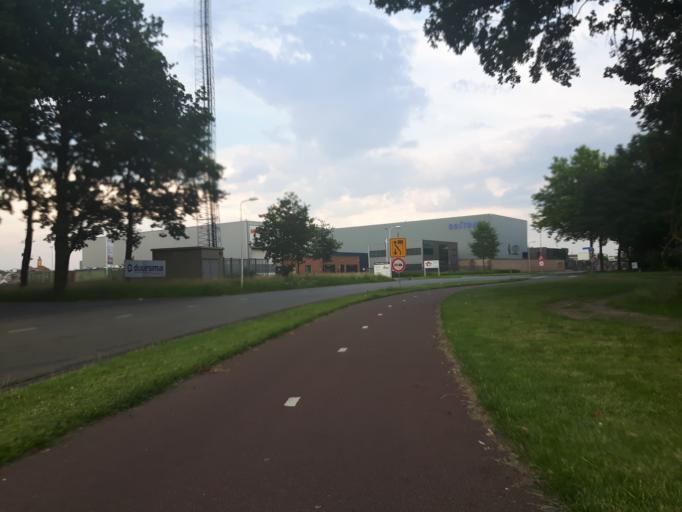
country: NL
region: Overijssel
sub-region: Gemeente Enschede
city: Enschede
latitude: 52.2238
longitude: 6.8443
